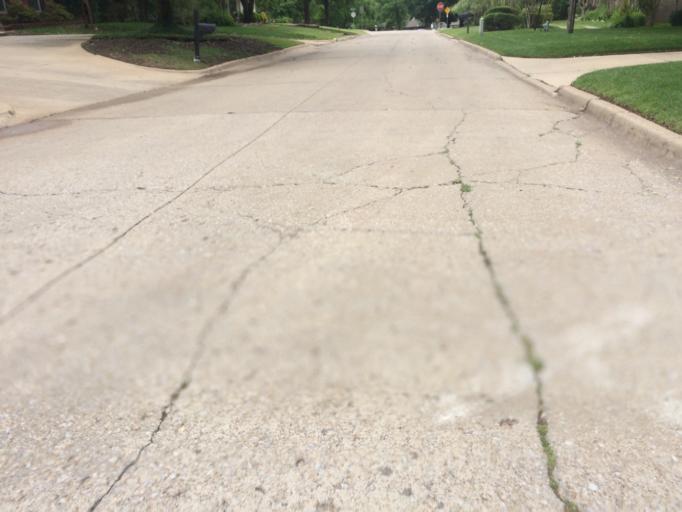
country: US
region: Oklahoma
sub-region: Cleveland County
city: Norman
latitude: 35.1903
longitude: -97.4568
